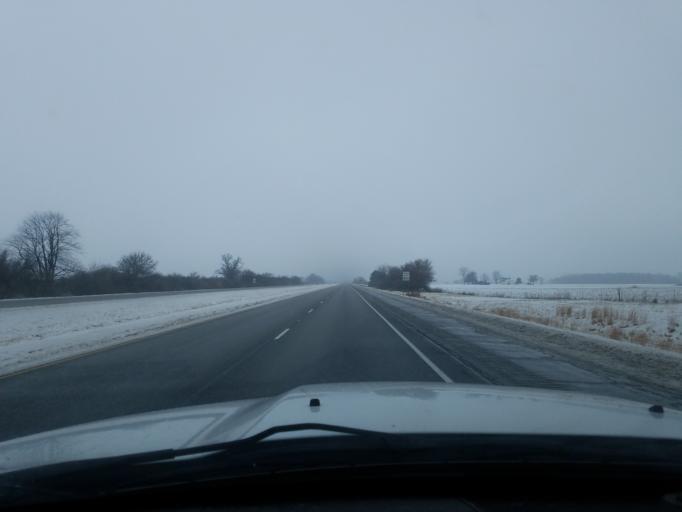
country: US
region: Indiana
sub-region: Fulton County
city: Rochester
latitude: 40.9836
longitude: -86.1679
